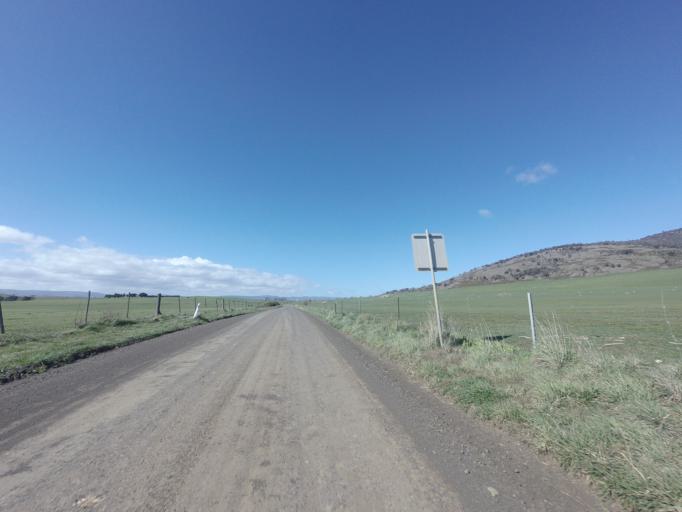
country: AU
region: Tasmania
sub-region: Northern Midlands
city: Evandale
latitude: -41.9175
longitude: 147.3892
